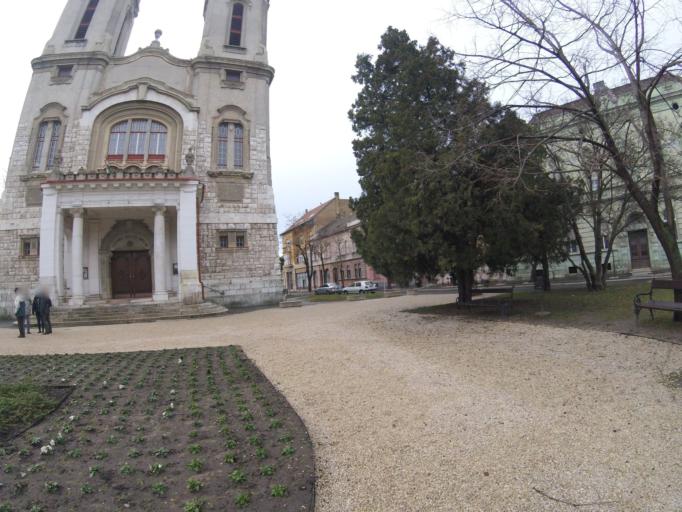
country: HU
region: Veszprem
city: Papa
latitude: 47.3282
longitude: 17.4694
